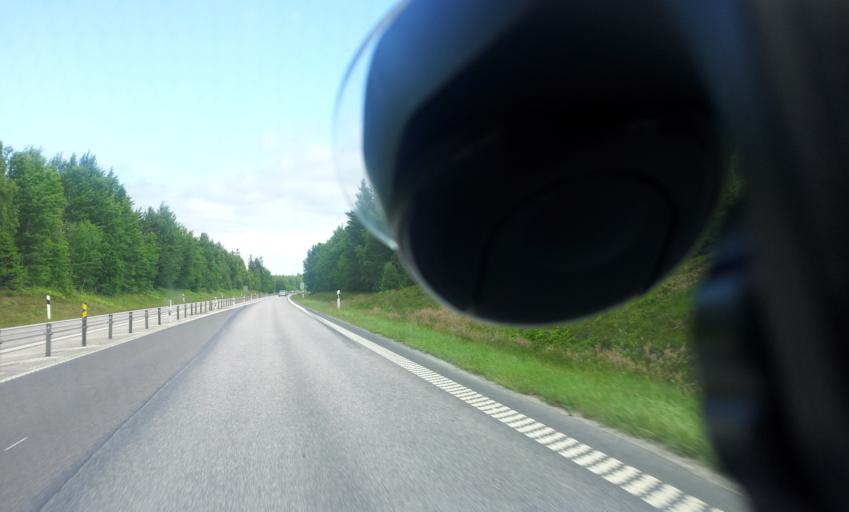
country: SE
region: Kalmar
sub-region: Kalmar Kommun
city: Lindsdal
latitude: 56.7391
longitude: 16.3079
